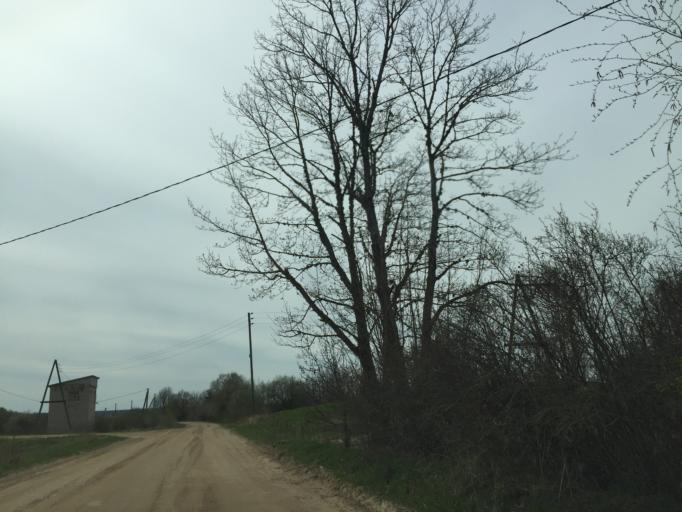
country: LV
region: Ludzas Rajons
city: Ludza
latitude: 56.5159
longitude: 27.5416
